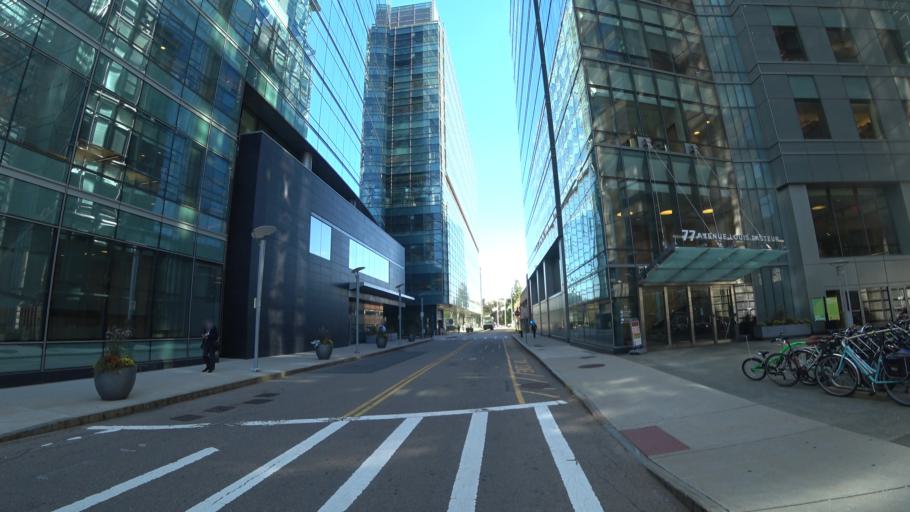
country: US
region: Massachusetts
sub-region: Norfolk County
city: Brookline
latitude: 42.3388
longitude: -71.1040
